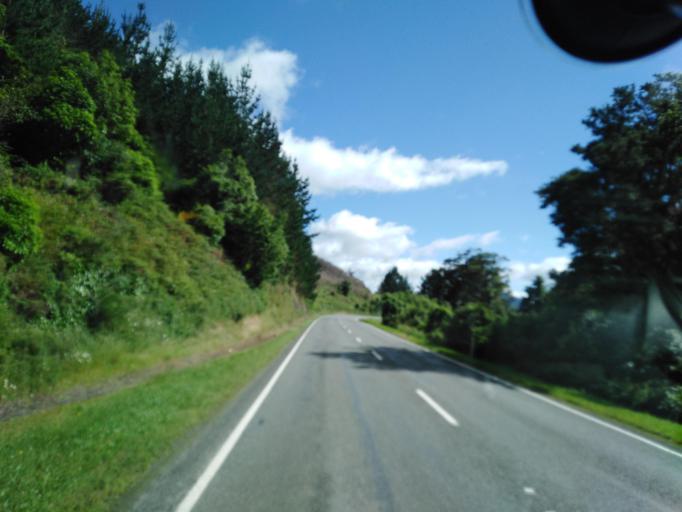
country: NZ
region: Nelson
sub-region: Nelson City
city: Nelson
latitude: -41.2567
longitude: 173.5761
